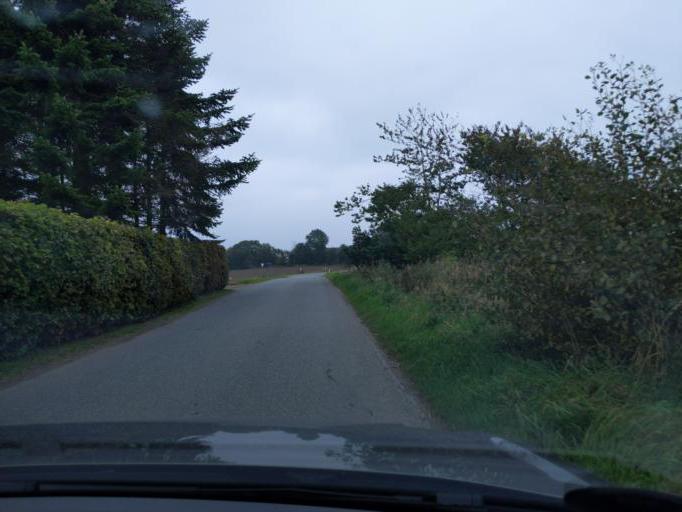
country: DK
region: Central Jutland
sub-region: Viborg Kommune
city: Viborg
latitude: 56.3587
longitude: 9.3197
